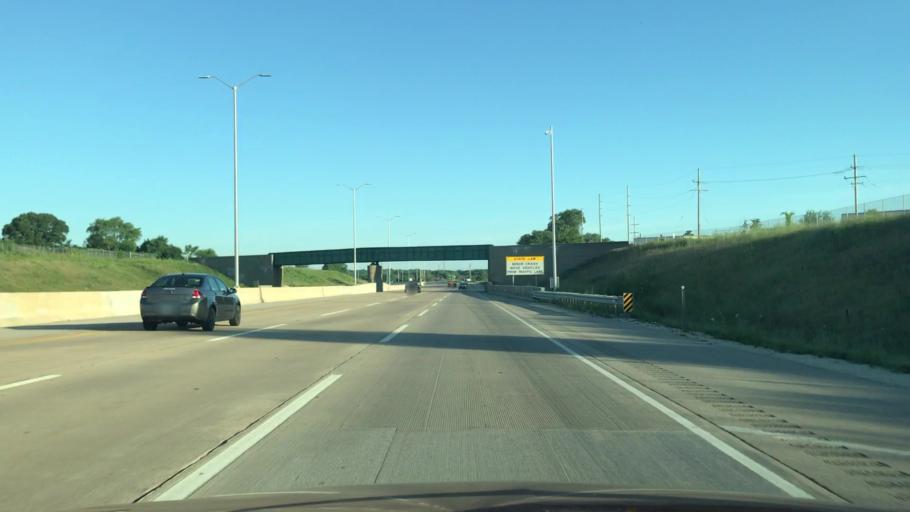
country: US
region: Illinois
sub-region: Winnebago County
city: Cherry Valley
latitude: 42.2416
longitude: -88.9203
